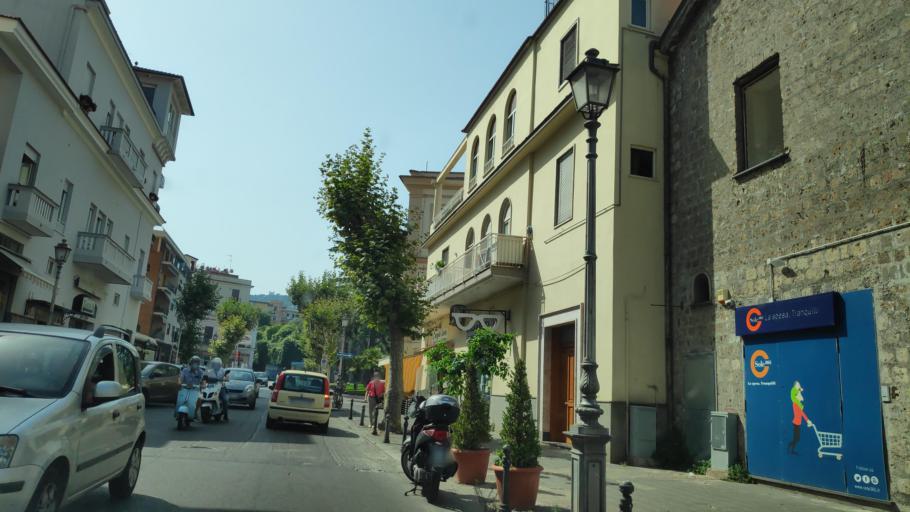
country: IT
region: Campania
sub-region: Provincia di Napoli
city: Sant'Agnello
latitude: 40.6312
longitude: 14.3989
